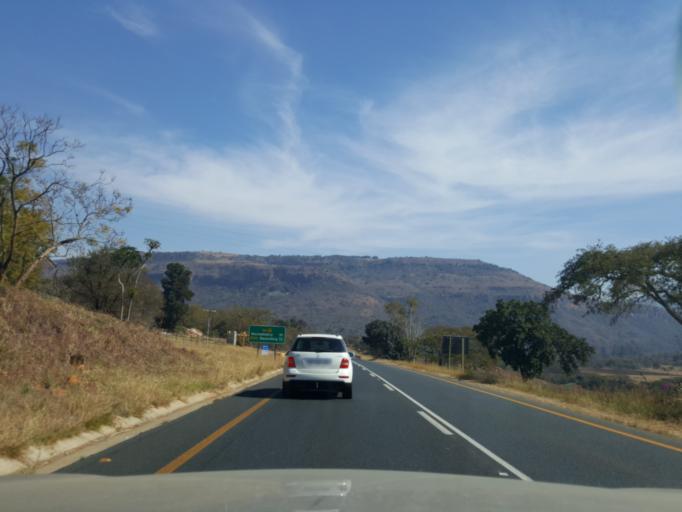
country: ZA
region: Mpumalanga
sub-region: Ehlanzeni District
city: Lydenburg
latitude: -25.3853
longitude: 30.5365
